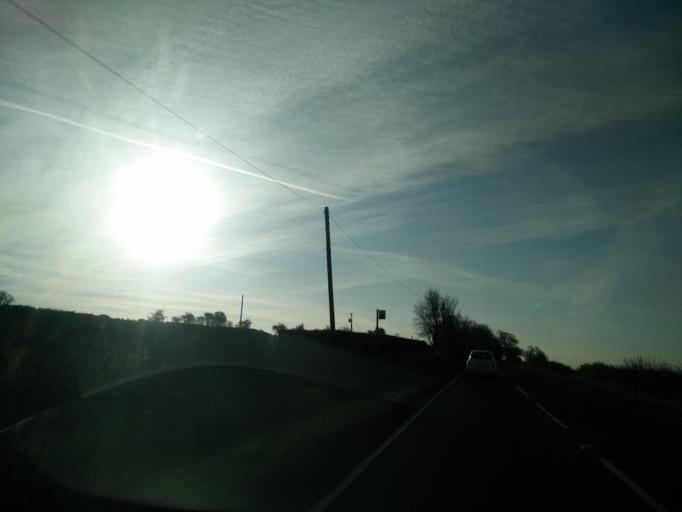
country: GB
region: England
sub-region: County Durham
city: Crook
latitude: 54.6776
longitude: -1.7253
